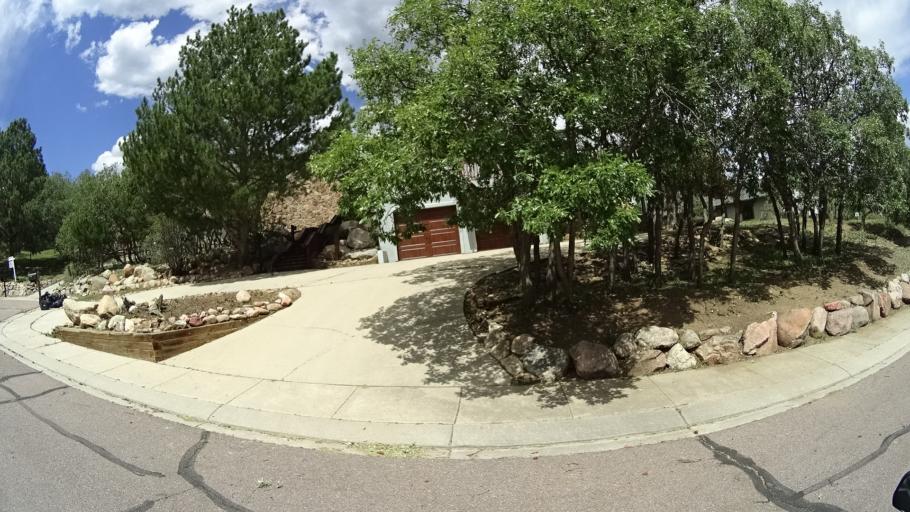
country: US
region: Colorado
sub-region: El Paso County
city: Stratmoor
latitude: 38.7697
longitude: -104.8212
